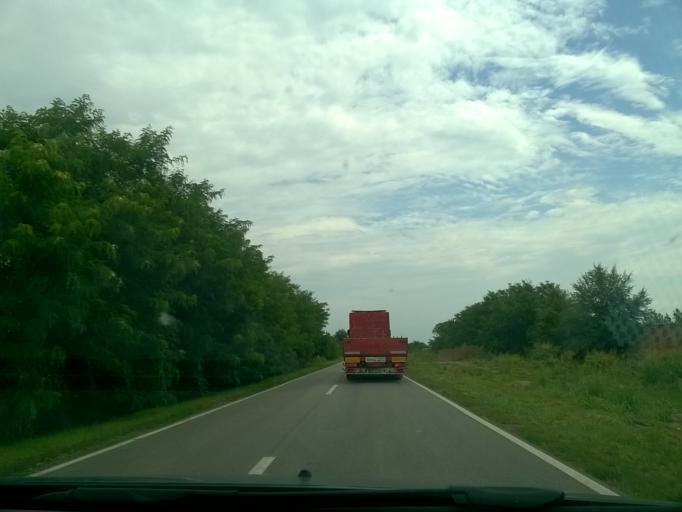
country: RS
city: Klek
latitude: 45.3850
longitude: 20.4640
